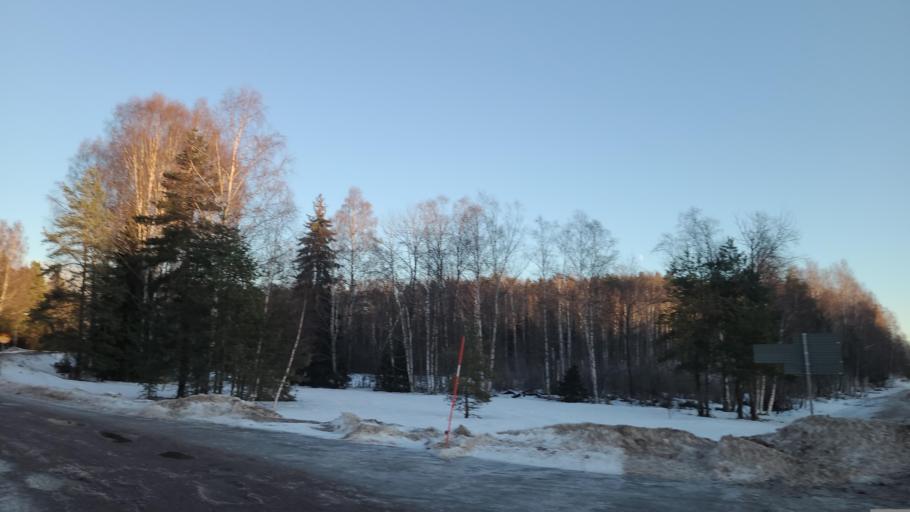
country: SE
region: Gaevleborg
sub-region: Soderhamns Kommun
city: Soderhamn
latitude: 61.2772
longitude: 16.9781
